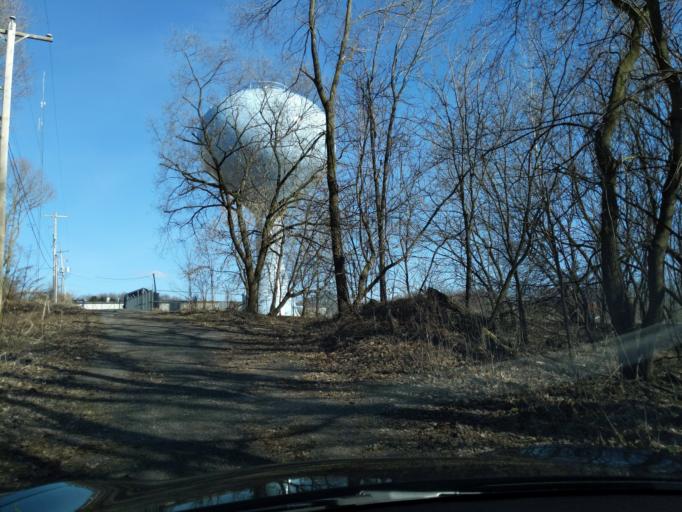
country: US
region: Michigan
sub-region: Ionia County
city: Saranac
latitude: 42.9249
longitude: -85.2054
